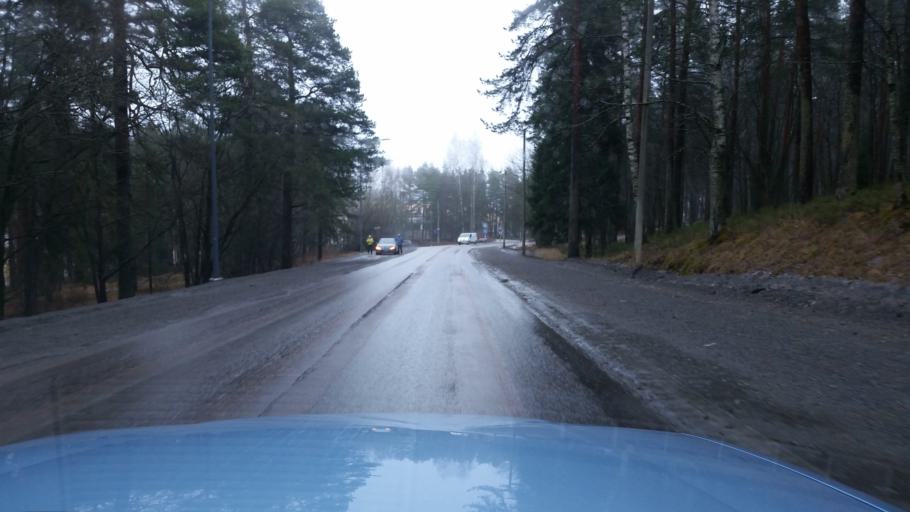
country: FI
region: Pirkanmaa
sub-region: Tampere
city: Tampere
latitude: 61.4976
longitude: 23.7291
